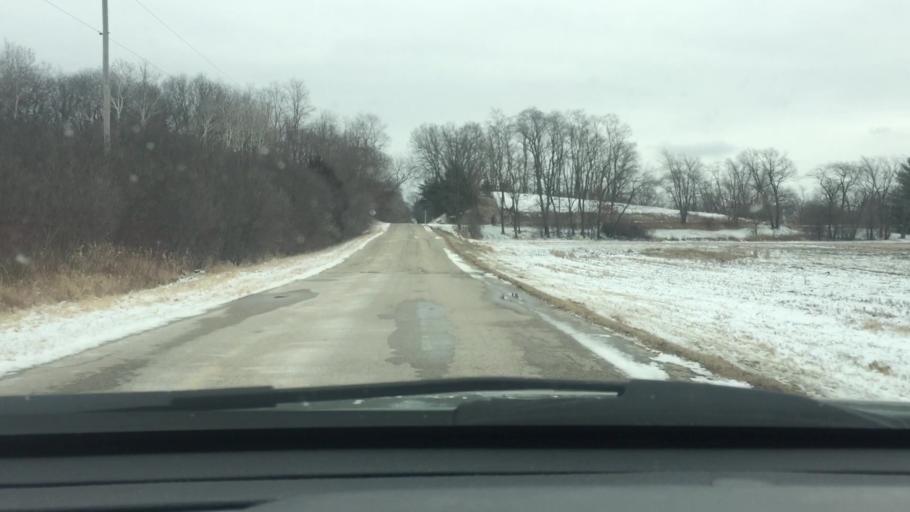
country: US
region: Wisconsin
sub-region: Jefferson County
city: Palmyra
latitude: 42.9006
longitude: -88.5707
